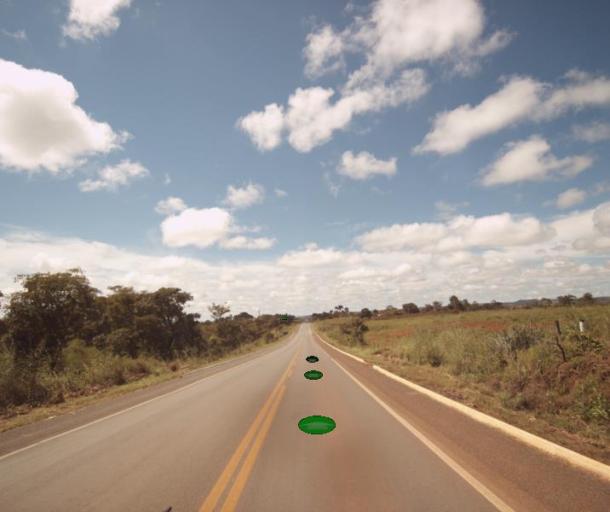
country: BR
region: Goias
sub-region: Padre Bernardo
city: Padre Bernardo
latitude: -15.1522
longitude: -48.3332
